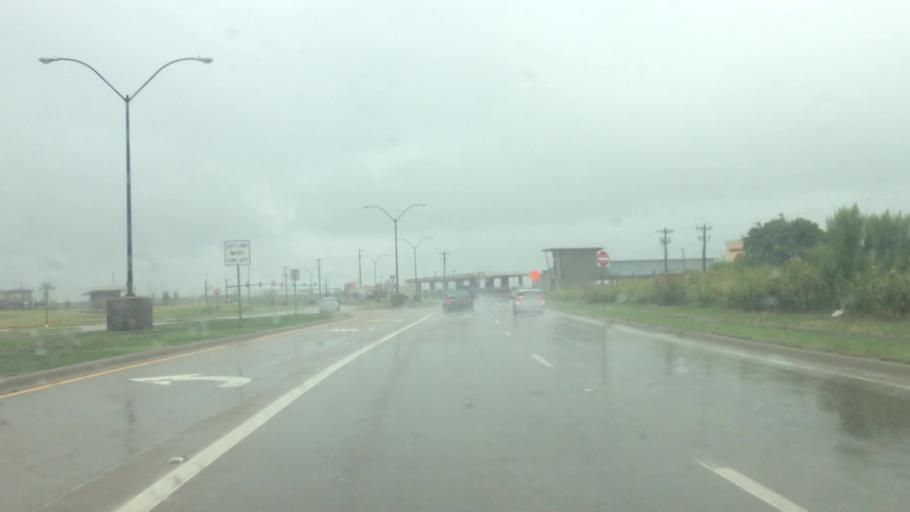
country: US
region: Texas
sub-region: Tarrant County
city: Keller
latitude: 32.9328
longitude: -97.3087
